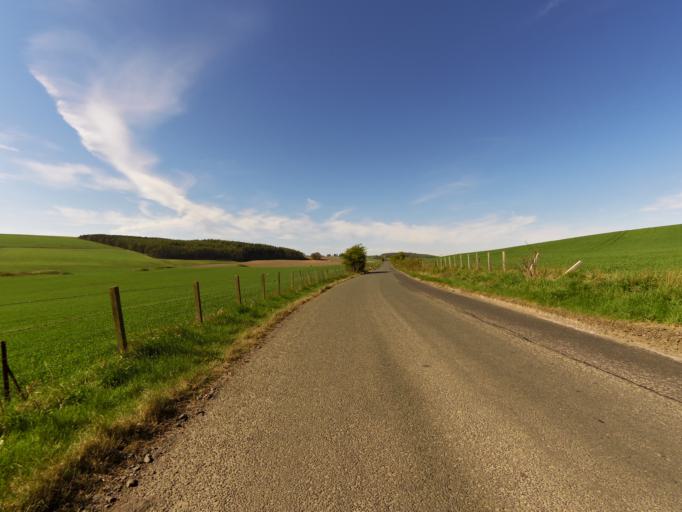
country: GB
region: Scotland
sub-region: Fife
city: Newport-On-Tay
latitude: 56.4124
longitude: -2.9884
